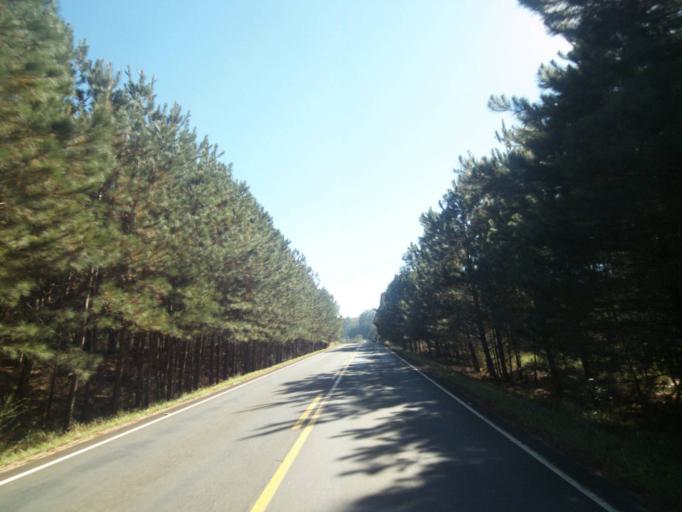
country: BR
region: Parana
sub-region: Telemaco Borba
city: Telemaco Borba
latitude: -24.4430
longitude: -50.5493
